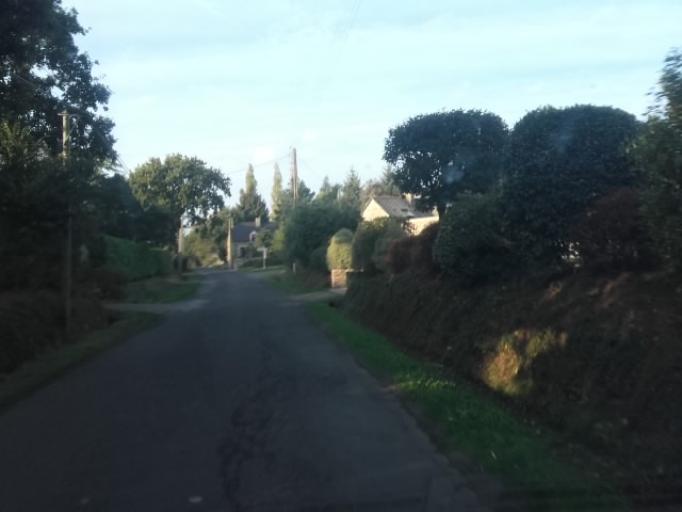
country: FR
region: Brittany
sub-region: Departement des Cotes-d'Armor
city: Pleguien
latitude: 48.6387
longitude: -2.9395
